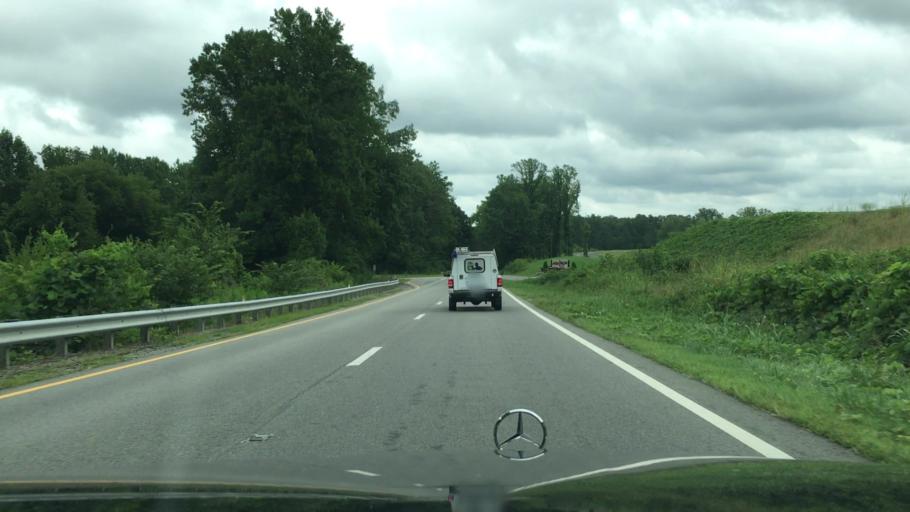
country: US
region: Virginia
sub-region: Prince Edward County
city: Hampden Sydney
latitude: 37.3119
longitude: -78.4946
